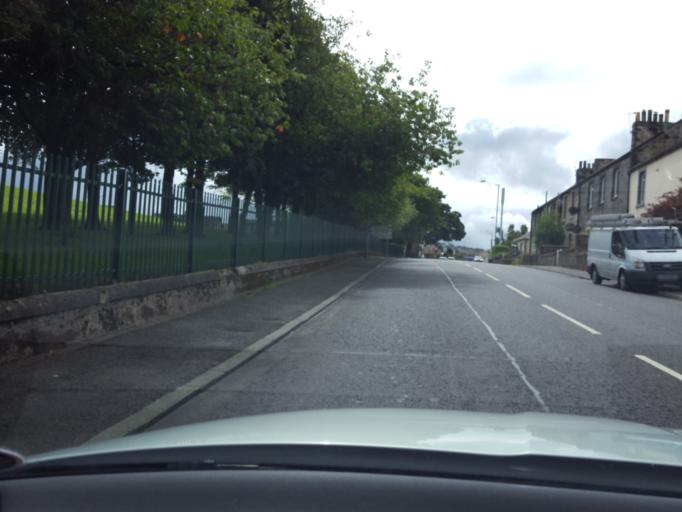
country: GB
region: Scotland
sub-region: Falkirk
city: Bo'ness
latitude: 56.0126
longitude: -3.6119
